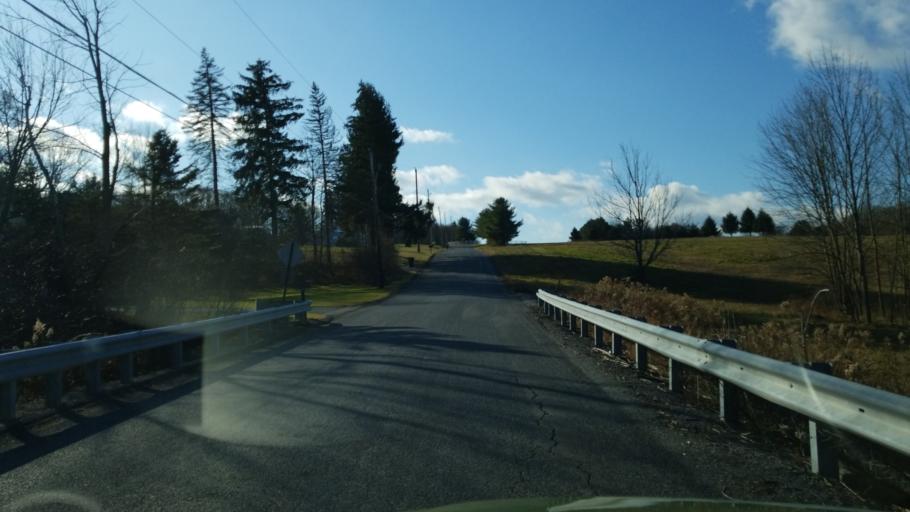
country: US
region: Pennsylvania
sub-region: Clearfield County
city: Clearfield
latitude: 41.0147
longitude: -78.4221
